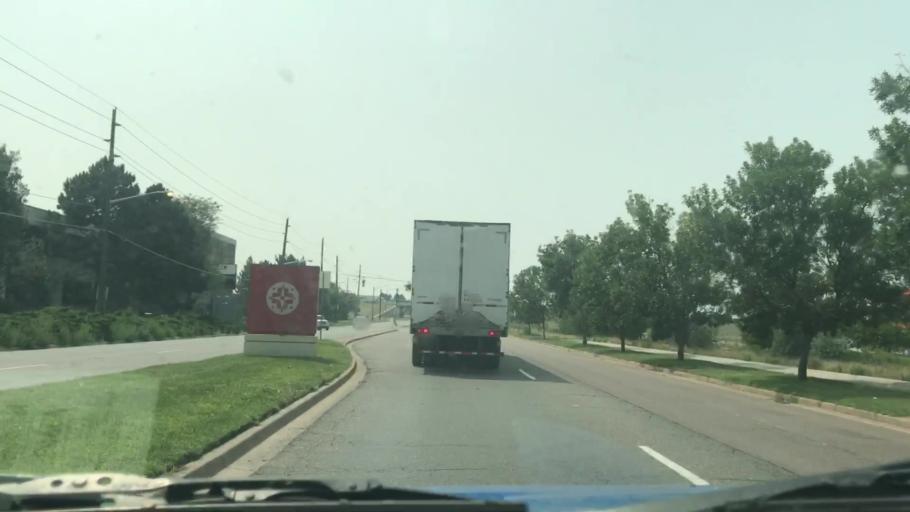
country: US
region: Colorado
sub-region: Adams County
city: Aurora
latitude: 39.7799
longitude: -104.8659
